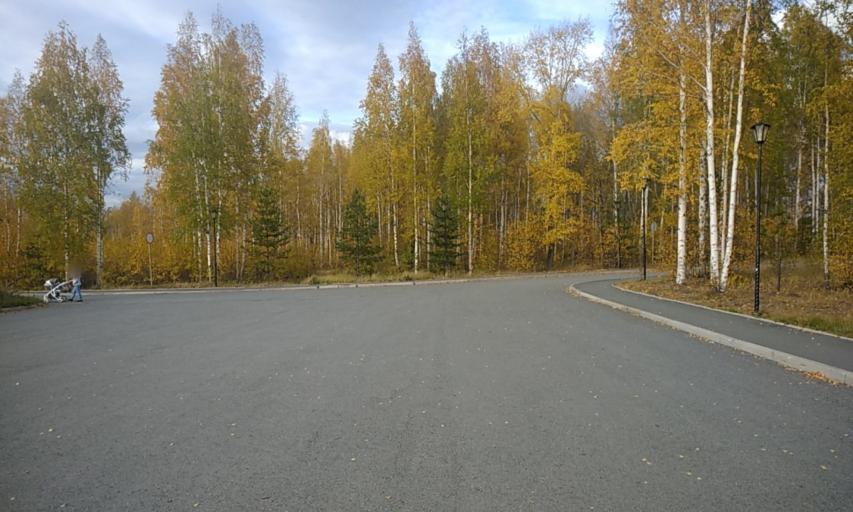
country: RU
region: Sverdlovsk
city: Krasnoural'sk
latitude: 58.3551
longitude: 60.0535
